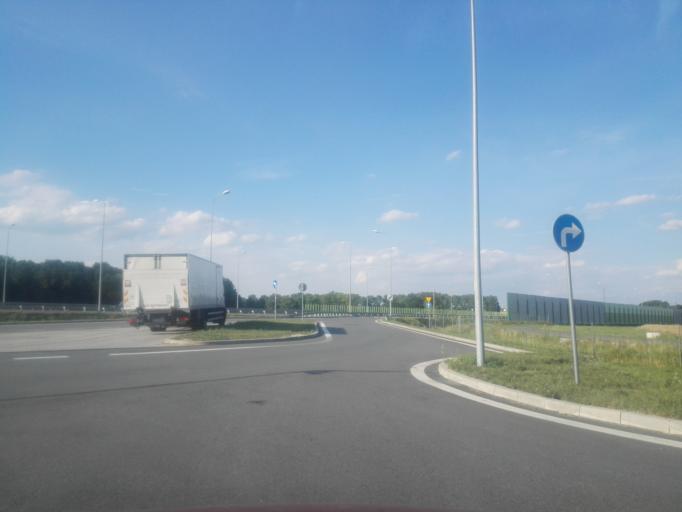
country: PL
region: Lower Silesian Voivodeship
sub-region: Powiat olesnicki
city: Sycow
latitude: 51.2947
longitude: 17.7355
